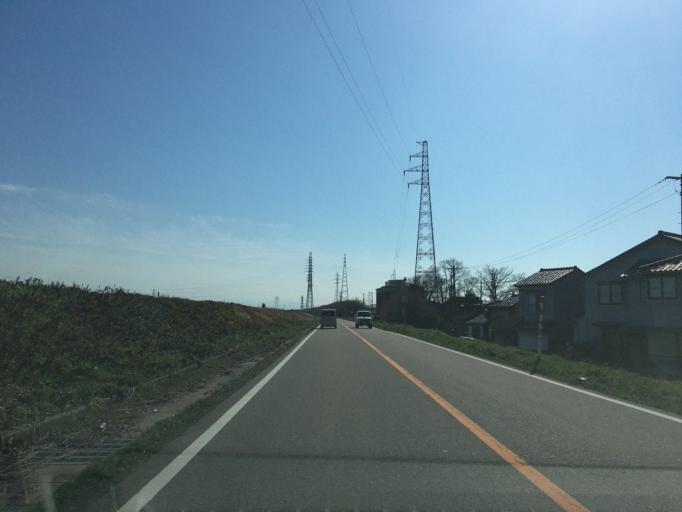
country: JP
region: Toyama
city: Nishishinminato
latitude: 36.7812
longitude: 137.0600
